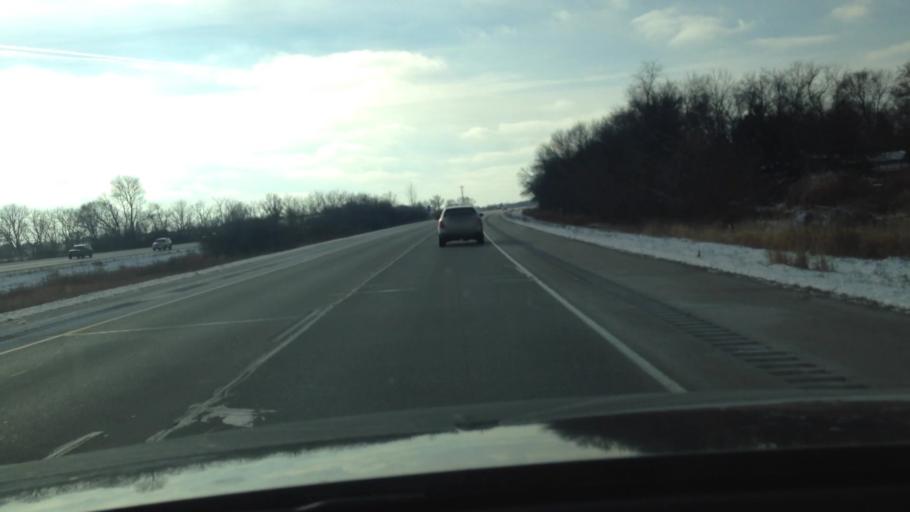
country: US
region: Wisconsin
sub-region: Waukesha County
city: Big Bend
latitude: 42.9153
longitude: -88.2060
